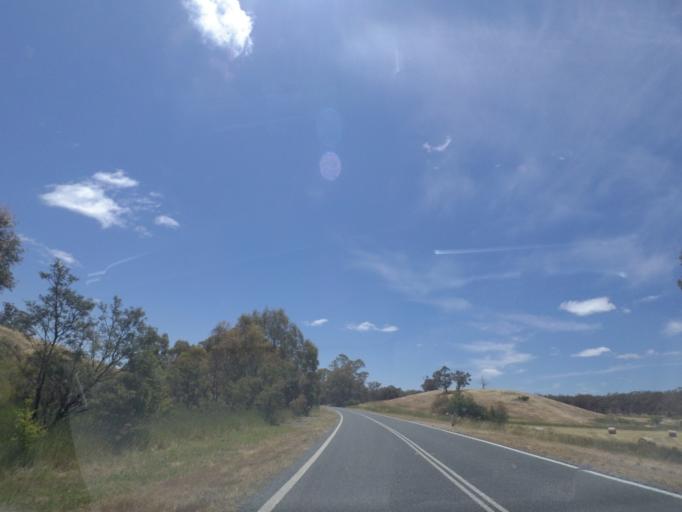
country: AU
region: Victoria
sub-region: Mount Alexander
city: Castlemaine
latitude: -37.1907
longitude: 144.1491
